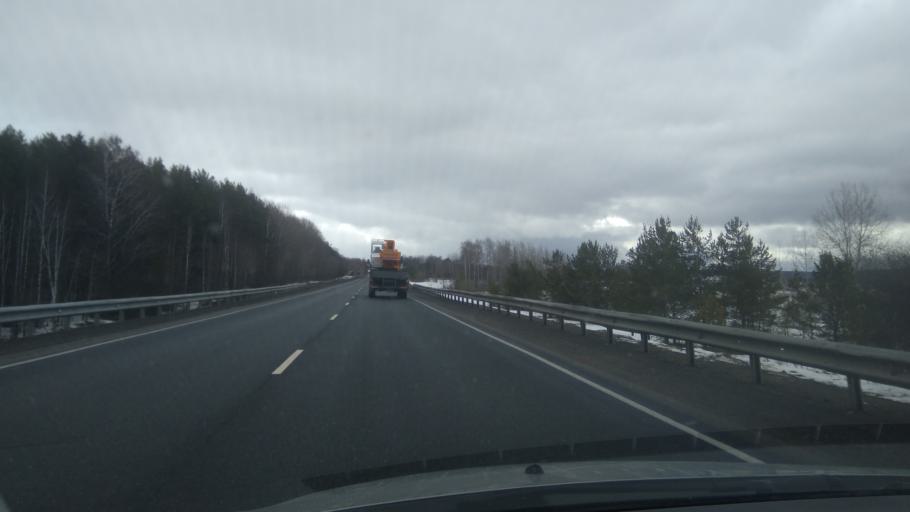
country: RU
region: Perm
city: Suksun
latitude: 57.0034
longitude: 57.4768
